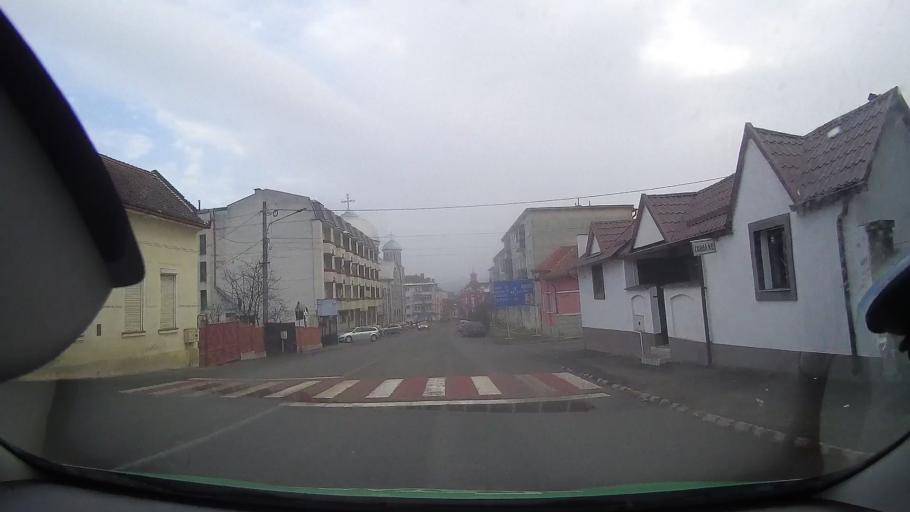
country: RO
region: Mures
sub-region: Municipiul Tarnaveni
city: Tarnaveni
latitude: 46.3338
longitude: 24.2865
